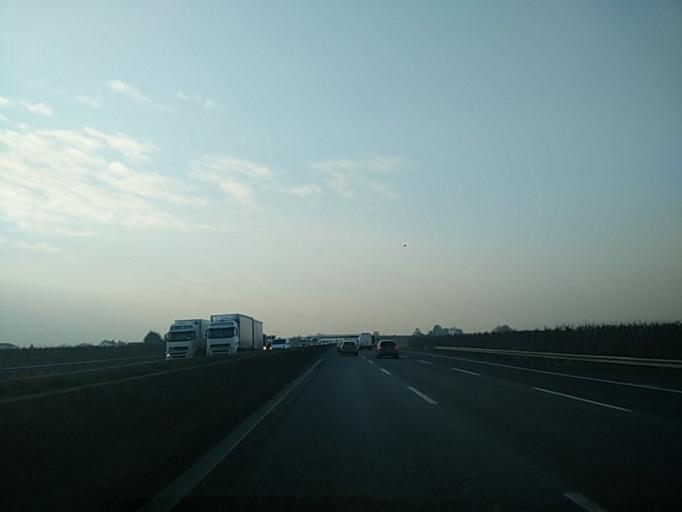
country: IT
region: Emilia-Romagna
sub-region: Provincia di Bologna
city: Bubano
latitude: 44.3710
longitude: 11.7694
